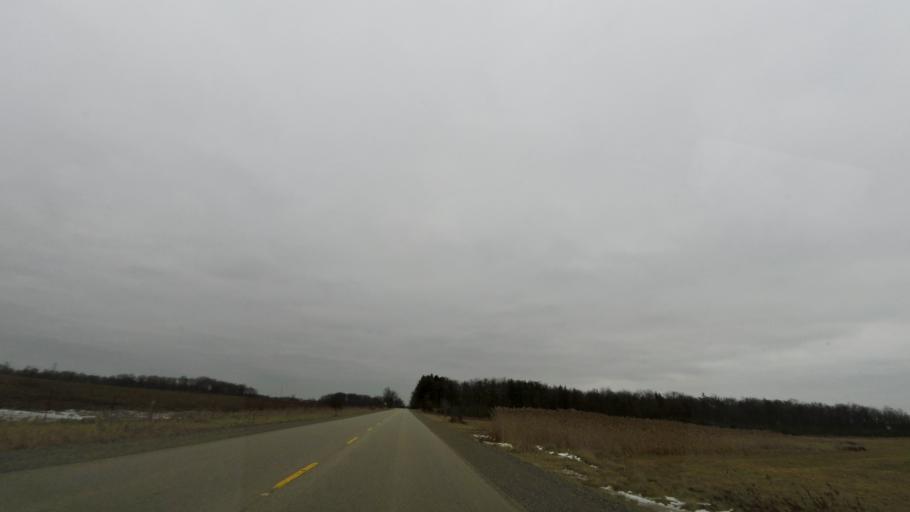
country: CA
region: Ontario
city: Brantford
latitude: 43.1098
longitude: -80.1548
